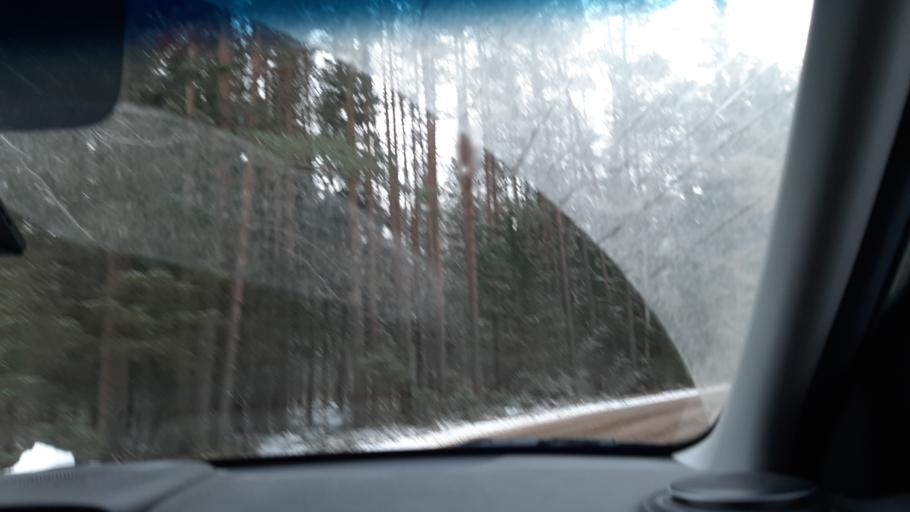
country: RU
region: Ivanovo
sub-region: Gorod Ivanovo
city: Ivanovo
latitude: 56.9166
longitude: 41.0050
